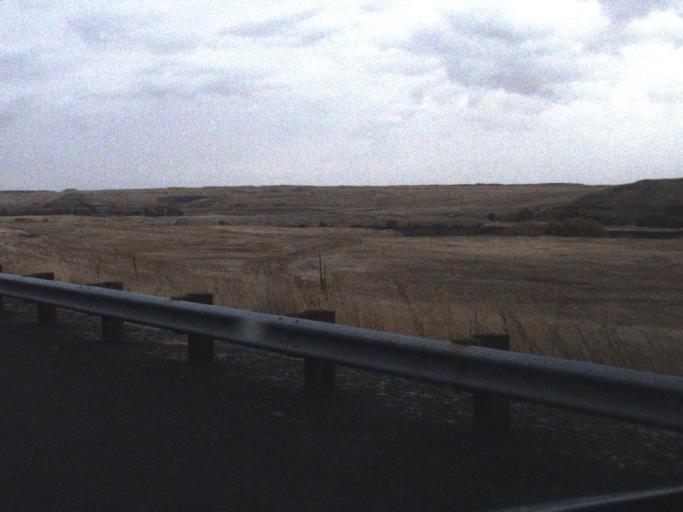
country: US
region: Washington
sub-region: Adams County
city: Ritzville
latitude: 46.7555
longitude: -118.1777
